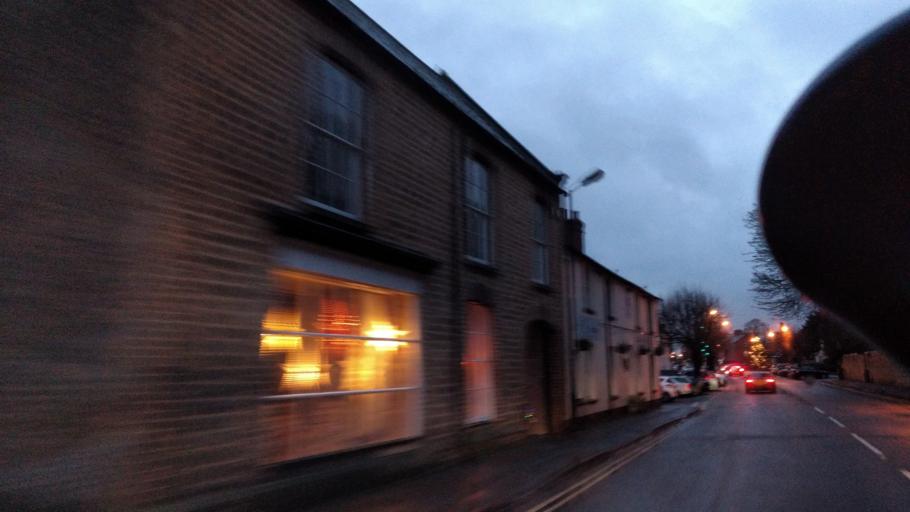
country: GB
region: England
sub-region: Oxfordshire
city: Shrivenham
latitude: 51.5994
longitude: -1.6518
